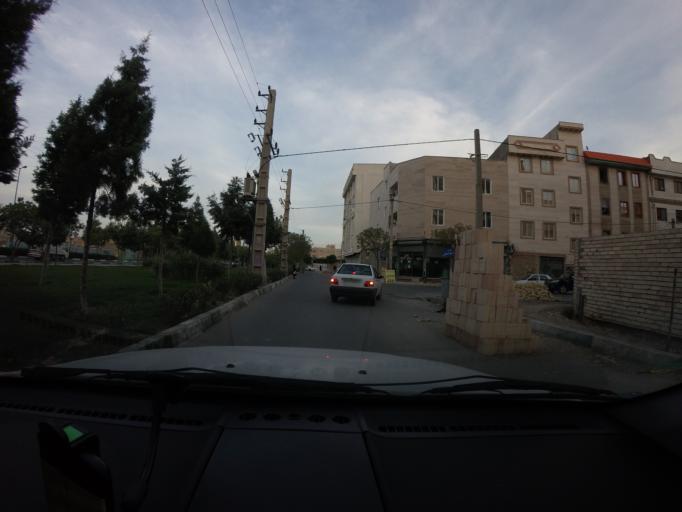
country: IR
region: Tehran
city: Eslamshahr
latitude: 35.5343
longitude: 51.2157
